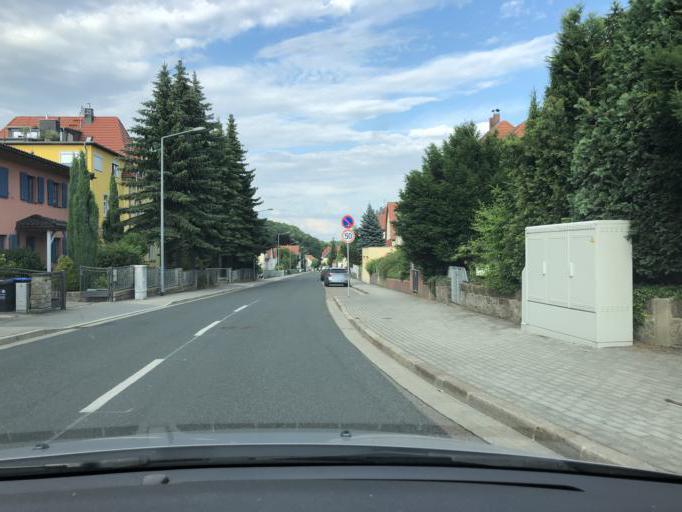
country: DE
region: Saxony
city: Freital
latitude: 51.0154
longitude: 13.6513
